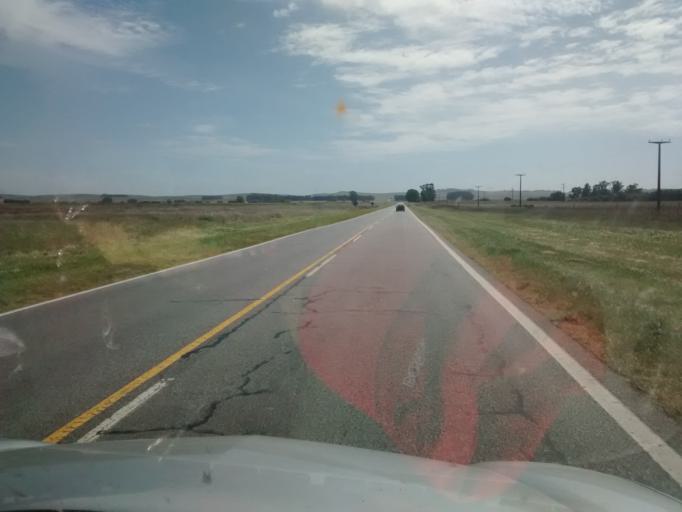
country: AR
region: Buenos Aires
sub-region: Partido de Balcarce
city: Balcarce
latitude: -37.6675
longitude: -58.5455
